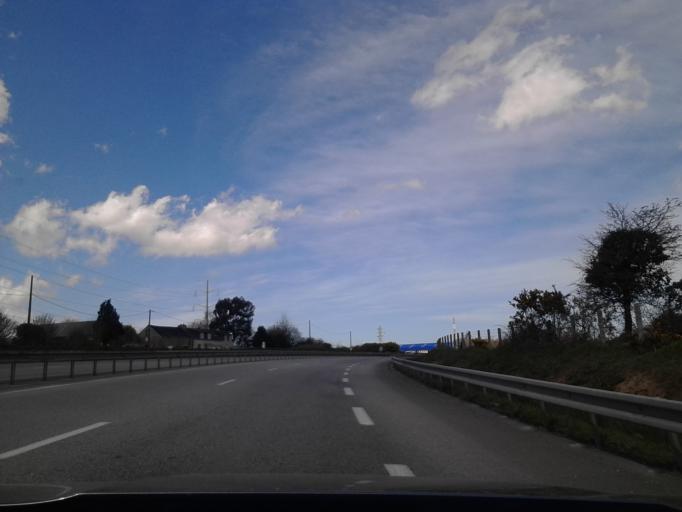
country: FR
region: Lower Normandy
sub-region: Departement de la Manche
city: La Glacerie
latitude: 49.5861
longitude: -1.5954
